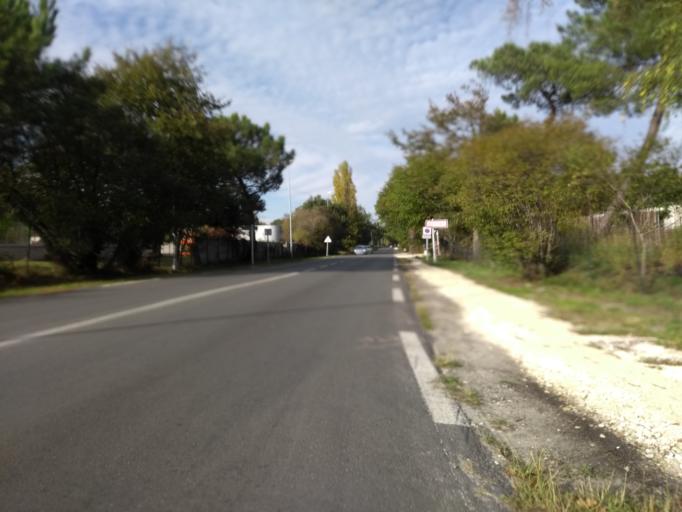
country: FR
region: Aquitaine
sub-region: Departement de la Gironde
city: Canejan
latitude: 44.7785
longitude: -0.6628
